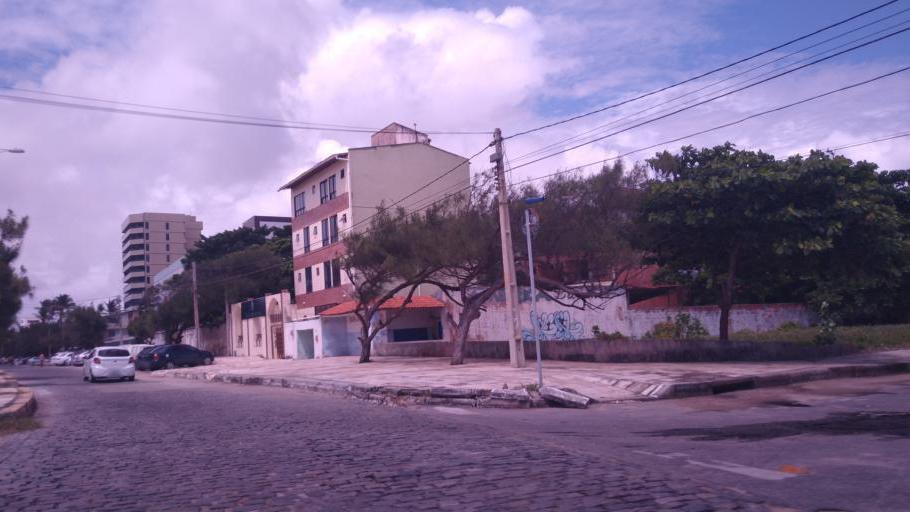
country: BR
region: Ceara
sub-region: Fortaleza
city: Fortaleza
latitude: -3.7309
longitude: -38.4579
